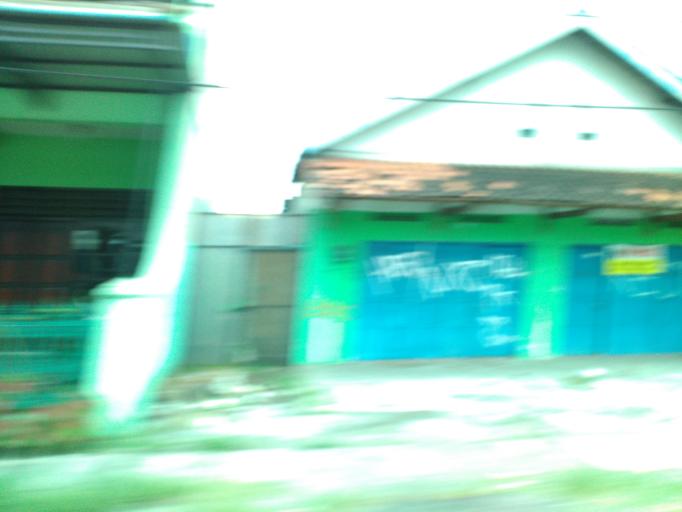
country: ID
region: Central Java
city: Gatak
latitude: -7.5982
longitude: 110.7034
